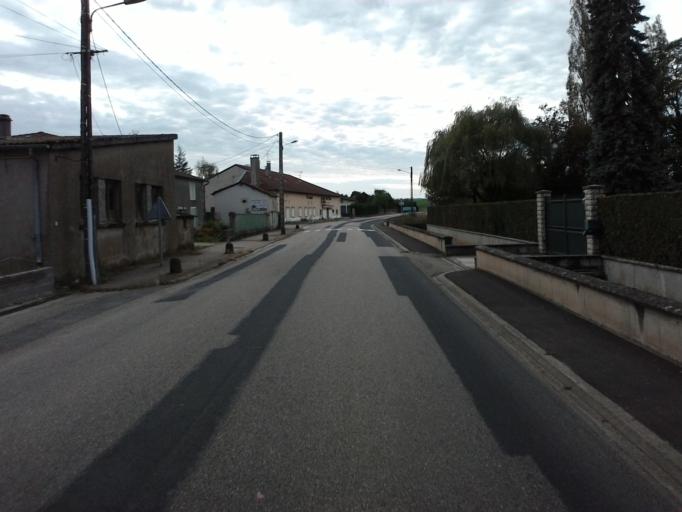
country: FR
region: Lorraine
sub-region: Departement de Meurthe-et-Moselle
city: Ecrouves
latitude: 48.7649
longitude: 5.8639
